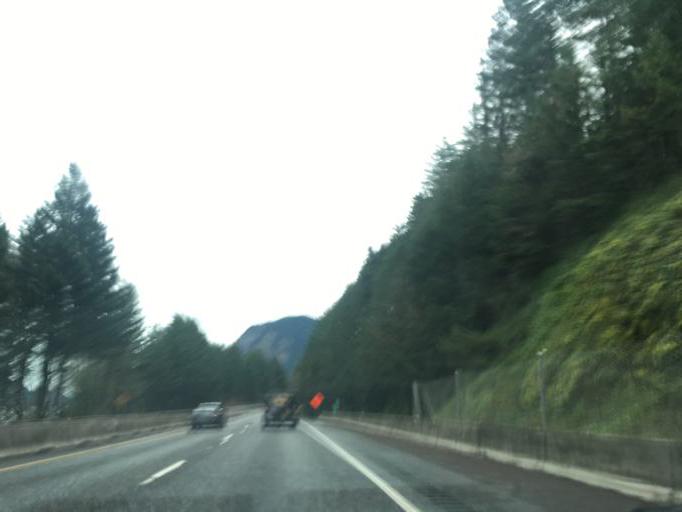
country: US
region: Washington
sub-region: Skamania County
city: Carson
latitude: 45.6930
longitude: -121.7887
